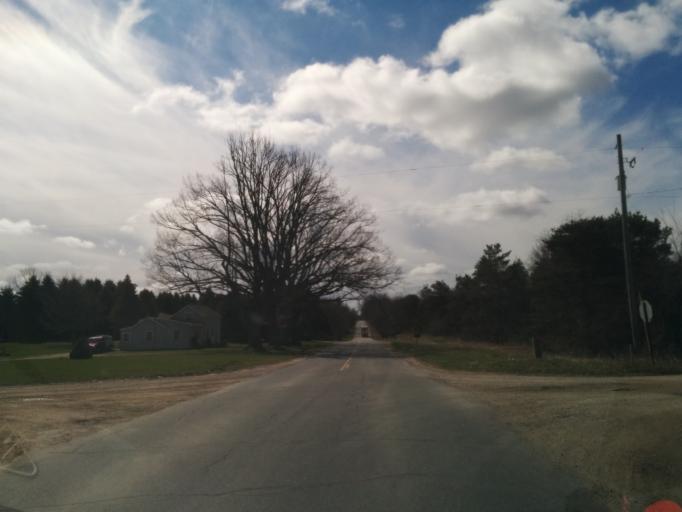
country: US
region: Michigan
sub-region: Newaygo County
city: Newaygo
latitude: 43.4178
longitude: -85.6423
